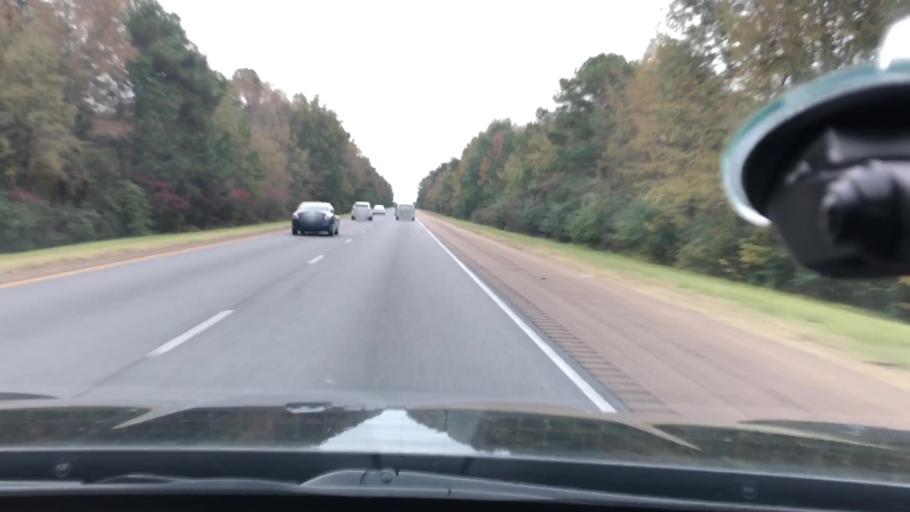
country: US
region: Arkansas
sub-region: Nevada County
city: Prescott
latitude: 33.8612
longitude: -93.3538
